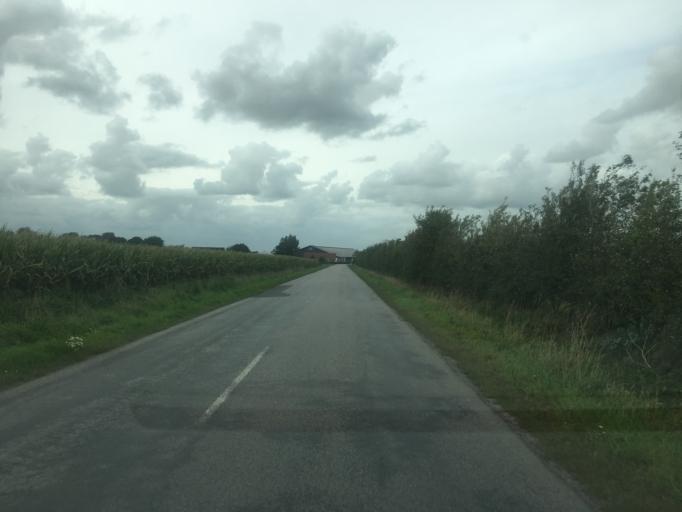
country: DE
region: Schleswig-Holstein
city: Aventoft
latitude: 54.9526
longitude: 8.8014
